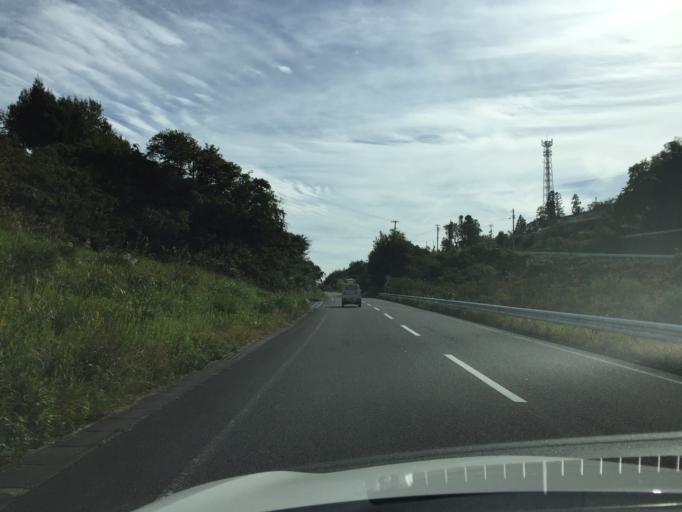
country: JP
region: Fukushima
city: Nihommatsu
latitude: 37.5567
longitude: 140.4993
